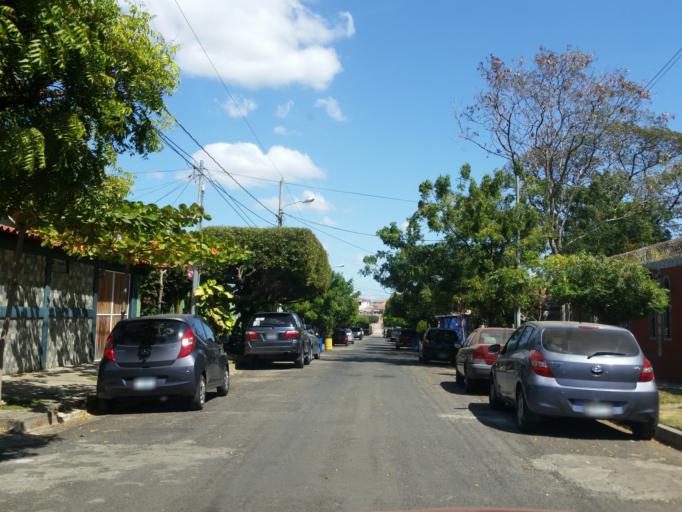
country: NI
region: Managua
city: Managua
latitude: 12.1100
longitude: -86.2453
